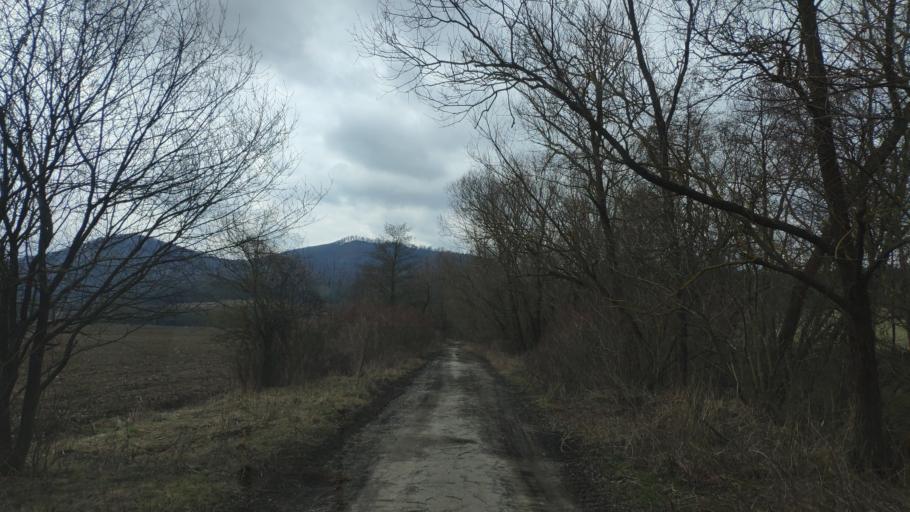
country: SK
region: Presovsky
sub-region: Okres Presov
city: Presov
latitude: 49.0814
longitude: 21.2865
